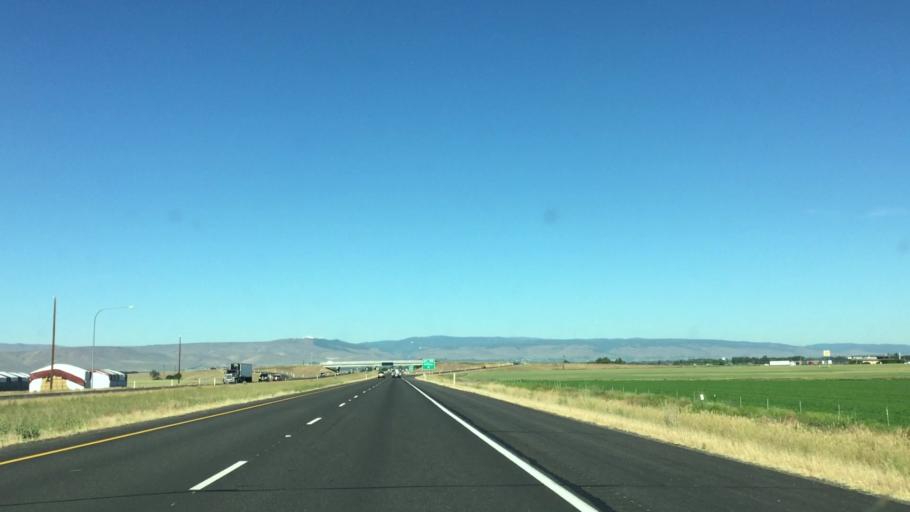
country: US
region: Washington
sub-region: Kittitas County
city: Kittitas
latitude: 46.9719
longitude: -120.4037
